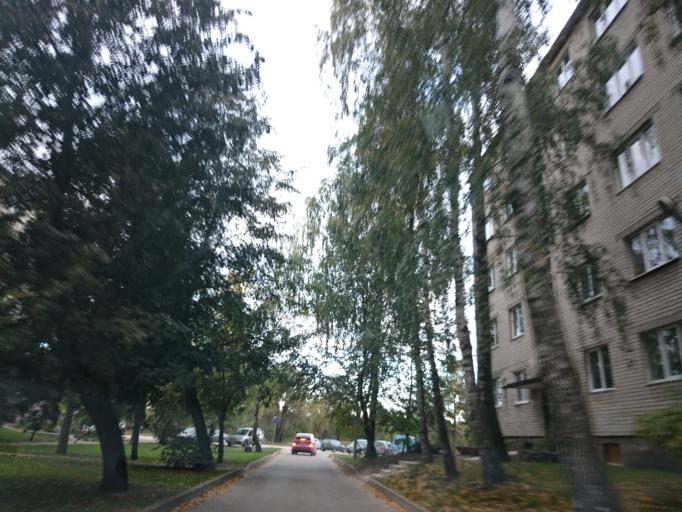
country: LV
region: Adazi
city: Adazi
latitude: 57.0799
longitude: 24.3285
